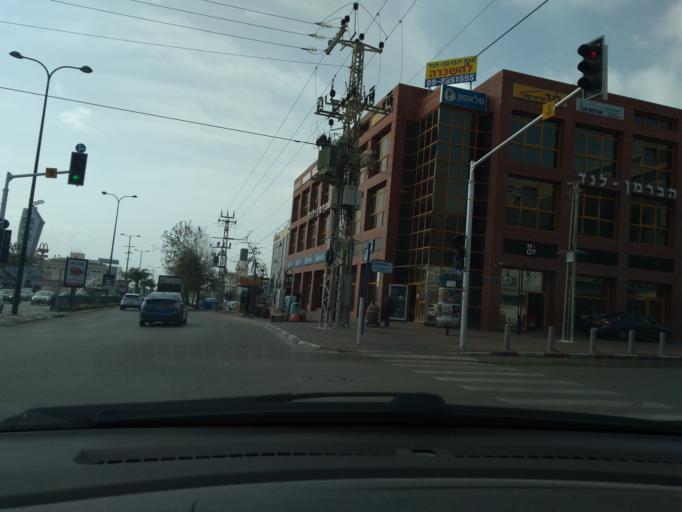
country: IL
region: Central District
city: Even Yehuda
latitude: 32.2781
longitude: 34.8601
